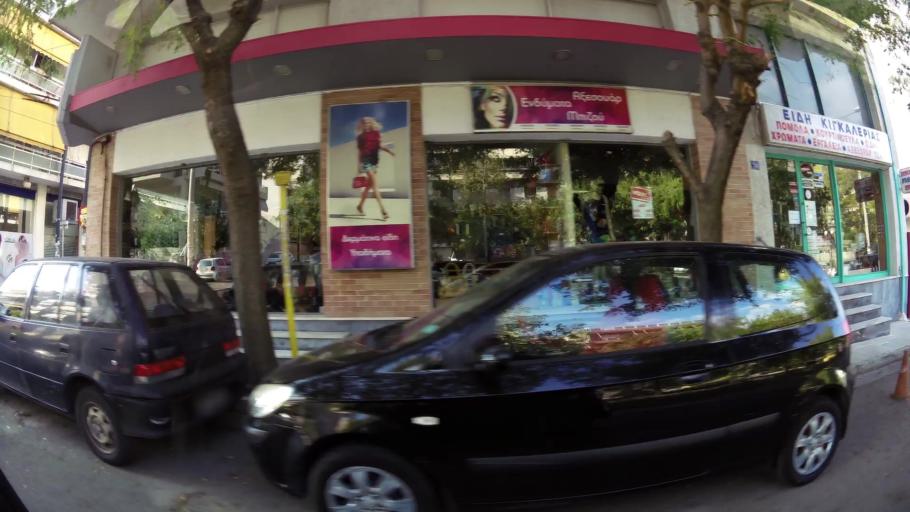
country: GR
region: Attica
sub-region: Nomarchia Athinas
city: Galatsi
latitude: 38.0238
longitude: 23.7466
